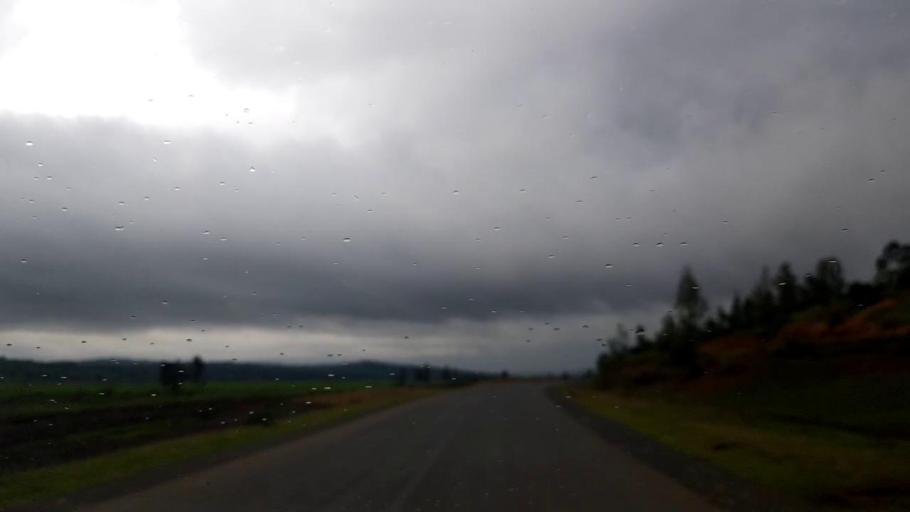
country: RW
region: Northern Province
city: Byumba
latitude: -1.4454
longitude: 30.2501
